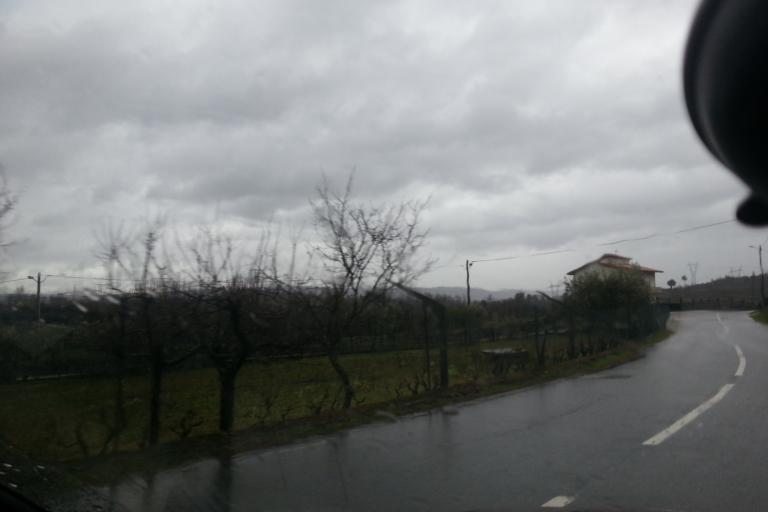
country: PT
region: Guarda
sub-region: Fornos de Algodres
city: Fornos de Algodres
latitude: 40.5702
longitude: -7.5118
